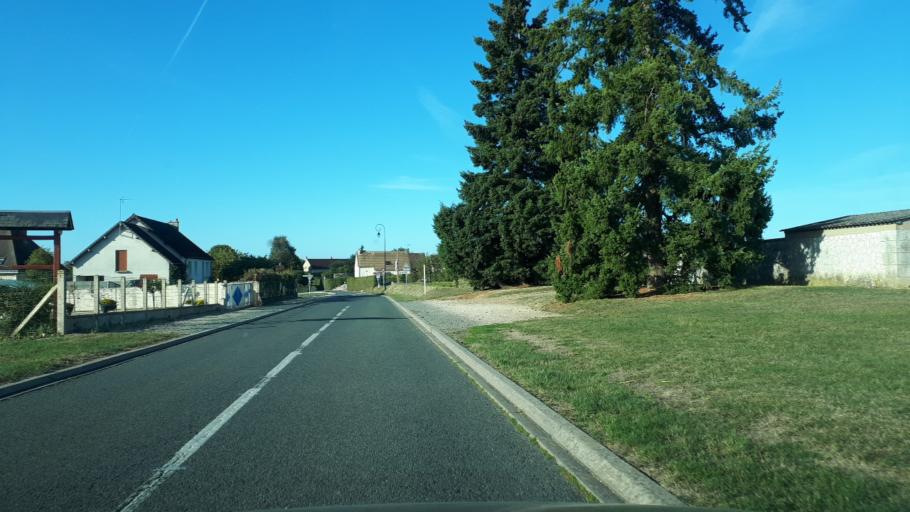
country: FR
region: Centre
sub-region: Departement du Loir-et-Cher
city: Lunay
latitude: 47.7566
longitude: 0.9386
